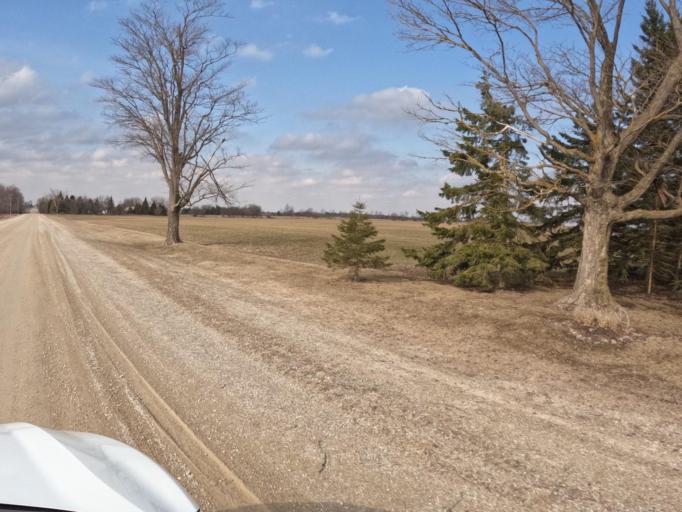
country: CA
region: Ontario
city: Shelburne
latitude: 43.9187
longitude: -80.3056
